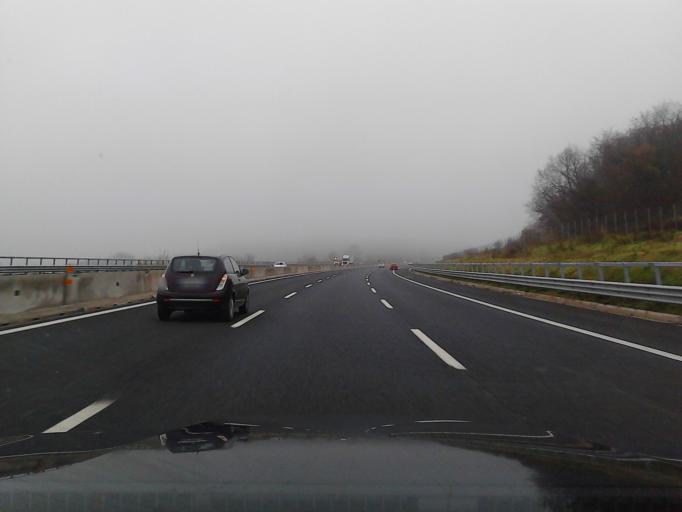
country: IT
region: The Marches
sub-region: Provincia di Pesaro e Urbino
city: Gradara
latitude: 43.9472
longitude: 12.7751
